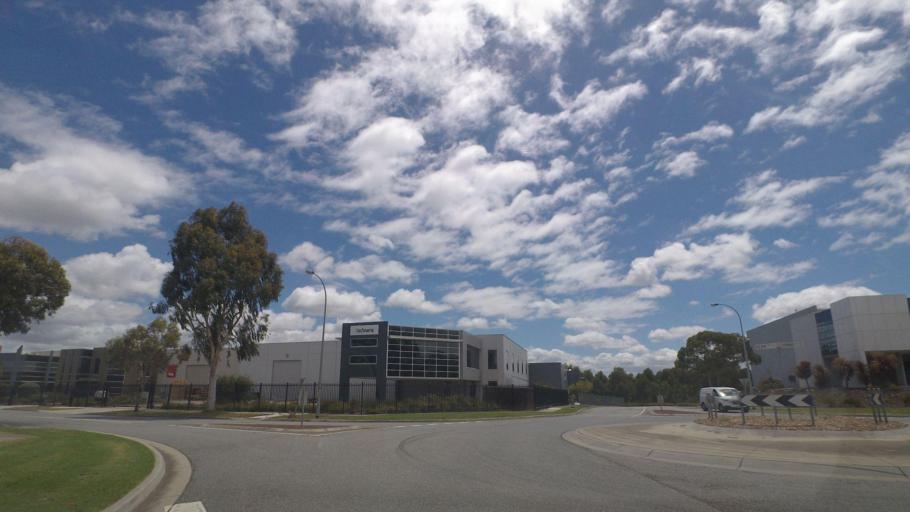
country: AU
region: Victoria
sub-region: Knox
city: Scoresby
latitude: -37.9063
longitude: 145.2426
